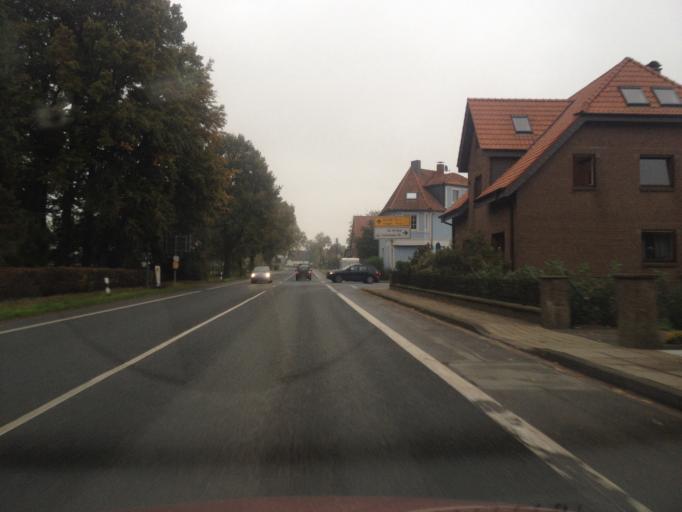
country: DE
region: North Rhine-Westphalia
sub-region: Regierungsbezirk Detmold
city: Bielefeld
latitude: 52.0717
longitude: 8.5787
